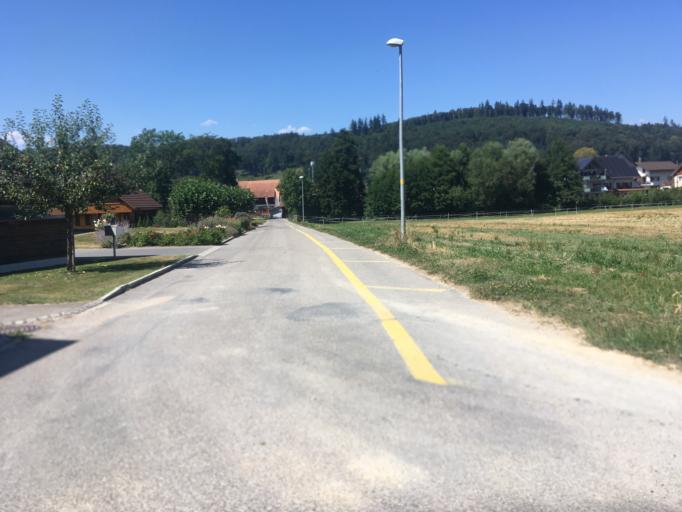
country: CH
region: Bern
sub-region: Seeland District
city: Grossaffoltern
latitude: 47.1130
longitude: 7.3583
